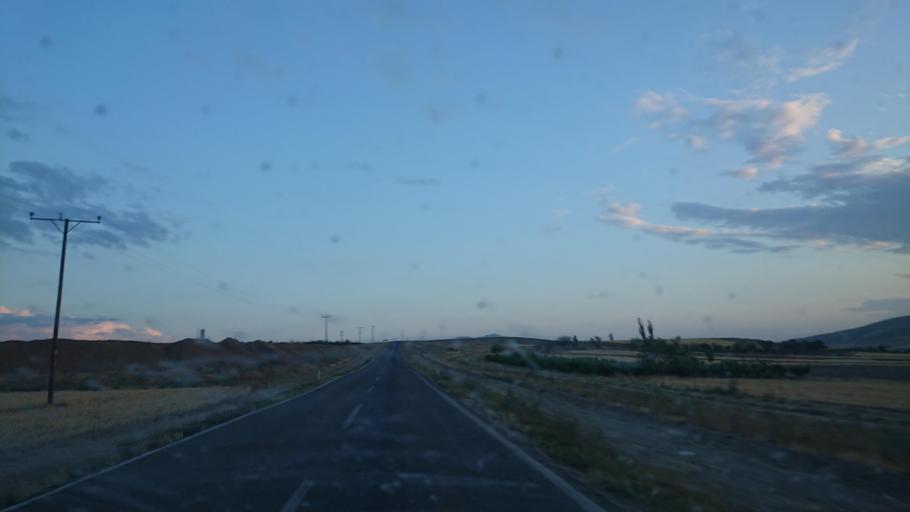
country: TR
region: Aksaray
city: Balci
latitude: 38.8042
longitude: 34.1305
